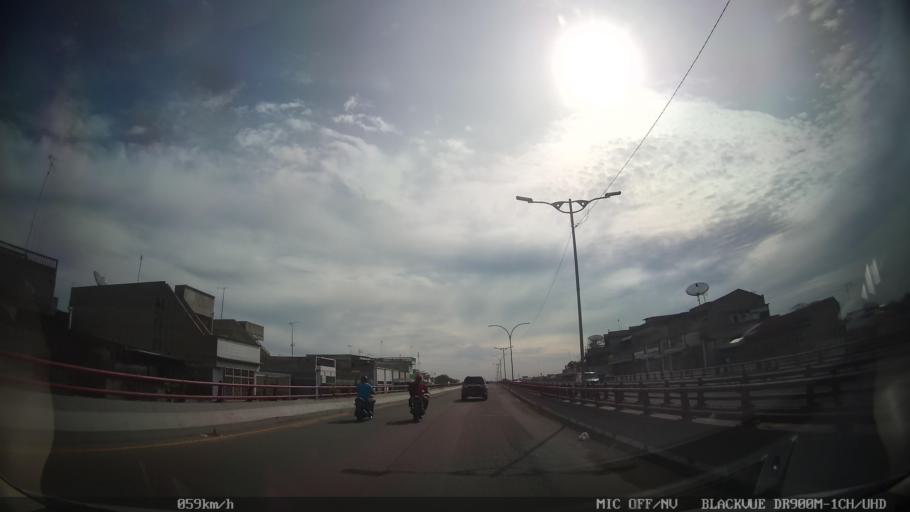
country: ID
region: North Sumatra
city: Medan
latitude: 3.6289
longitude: 98.6699
